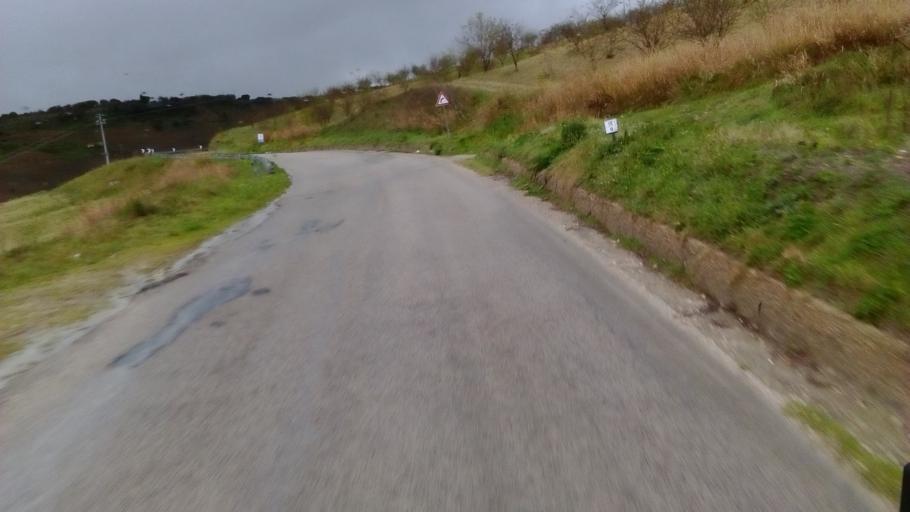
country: IT
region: Sicily
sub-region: Enna
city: Pietraperzia
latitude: 37.4421
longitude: 14.1769
